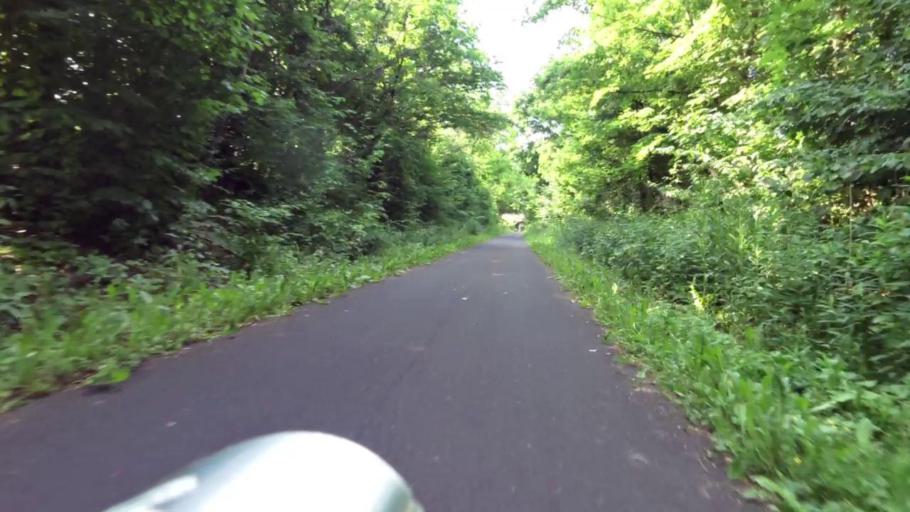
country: PL
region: Kujawsko-Pomorskie
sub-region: Powiat torunski
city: Lubianka
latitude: 53.0839
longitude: 18.5370
